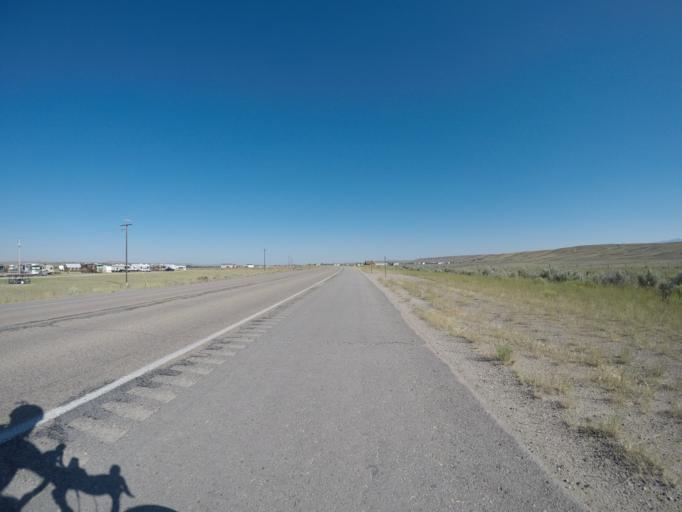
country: US
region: Wyoming
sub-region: Sublette County
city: Pinedale
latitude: 42.7599
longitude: -109.7335
